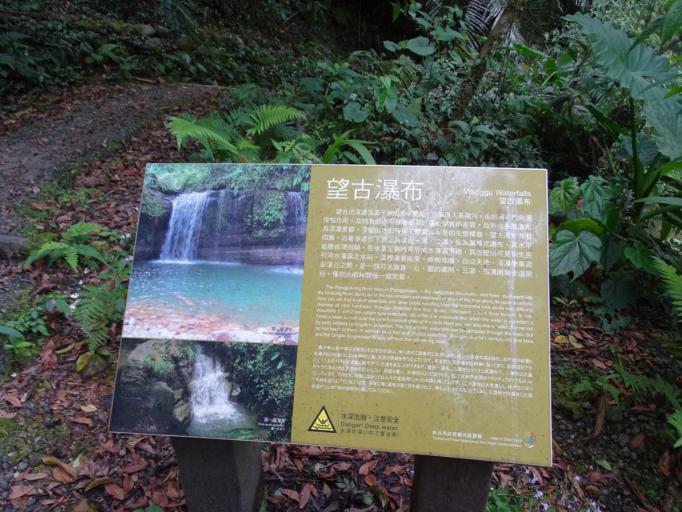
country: TW
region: Taiwan
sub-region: Keelung
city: Keelung
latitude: 25.0342
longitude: 121.7592
